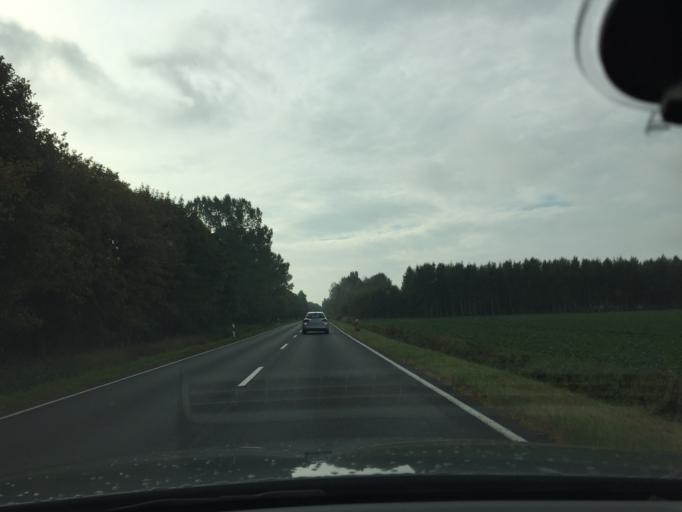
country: DE
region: Mecklenburg-Vorpommern
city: Ostseebad Dierhagen
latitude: 54.2355
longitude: 12.3634
